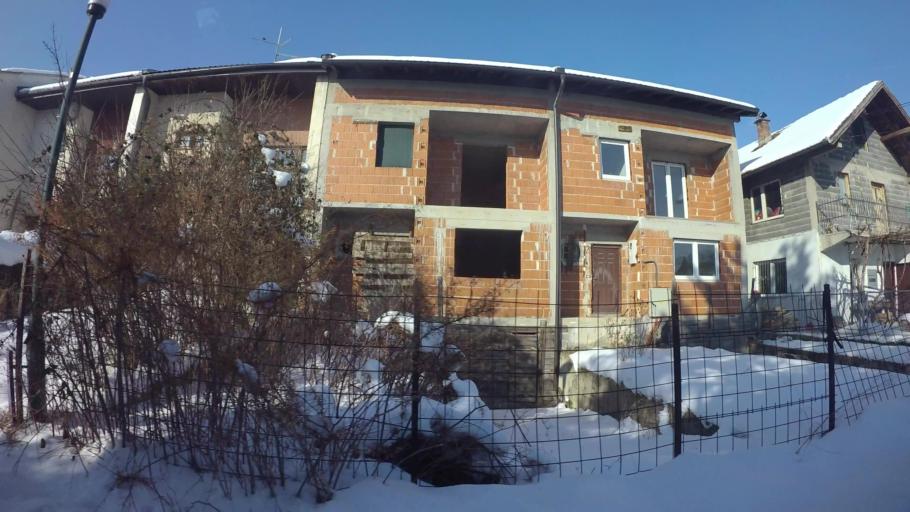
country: BA
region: Federation of Bosnia and Herzegovina
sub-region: Kanton Sarajevo
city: Sarajevo
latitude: 43.8153
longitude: 18.3184
